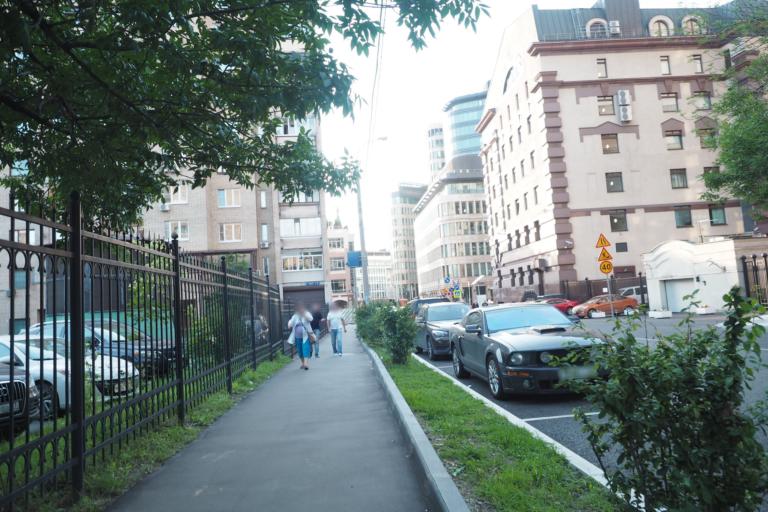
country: RU
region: Moskovskaya
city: Dorogomilovo
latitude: 55.7768
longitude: 37.5879
